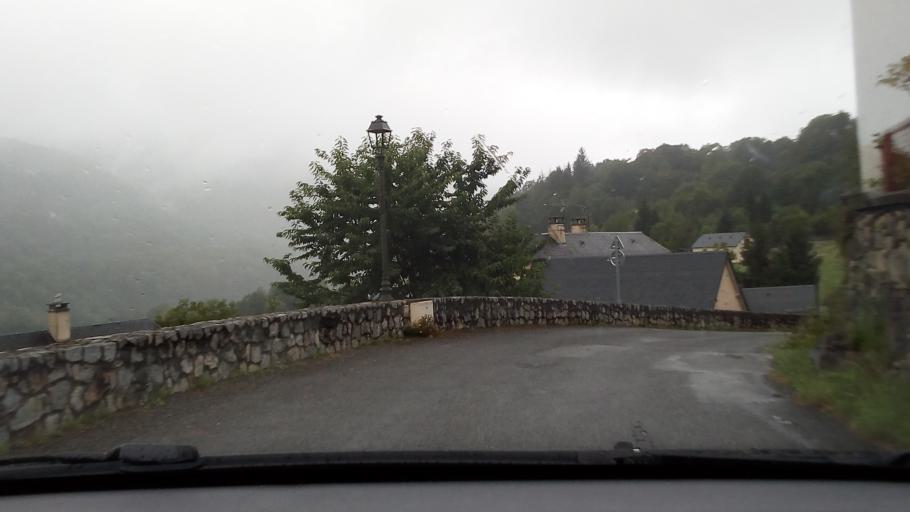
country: FR
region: Midi-Pyrenees
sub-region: Departement des Hautes-Pyrenees
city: Argeles-Gazost
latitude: 42.9906
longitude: -0.1253
